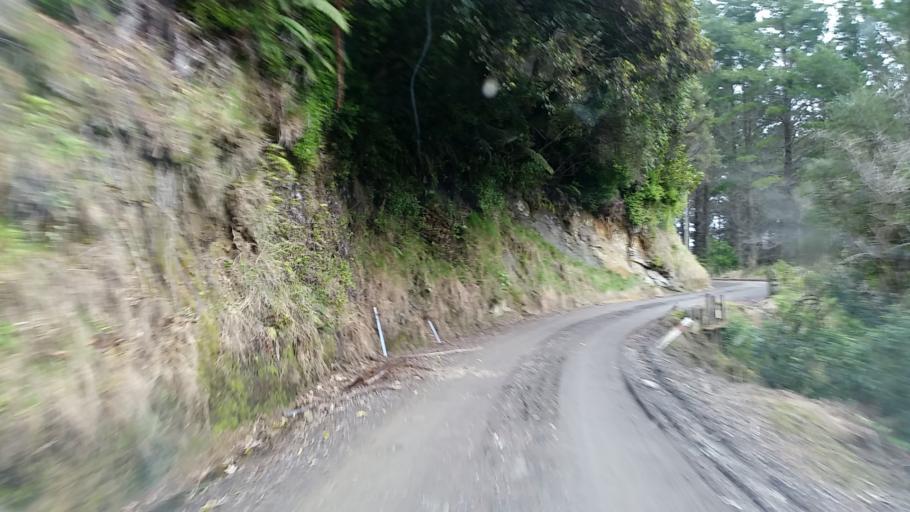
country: NZ
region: Taranaki
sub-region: New Plymouth District
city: Waitara
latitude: -39.1614
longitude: 174.5398
